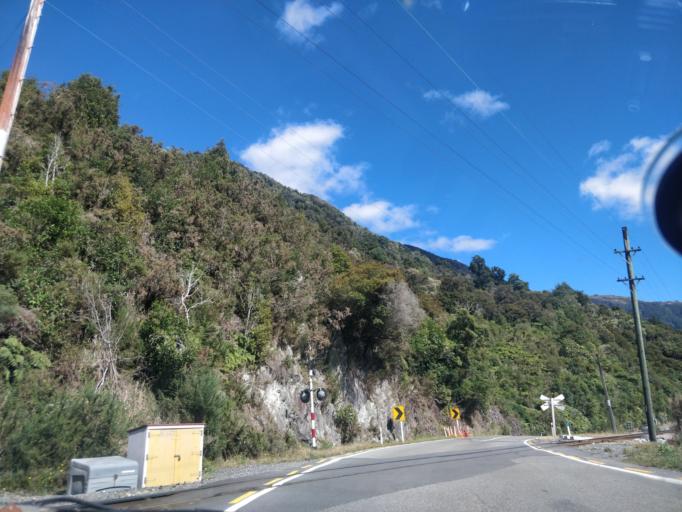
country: NZ
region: West Coast
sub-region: Grey District
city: Greymouth
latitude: -42.7636
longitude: 171.6031
